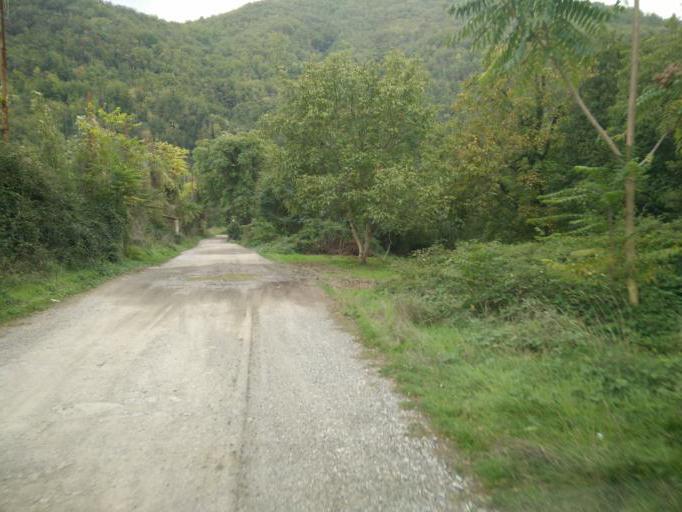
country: IT
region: Tuscany
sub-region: Provincia di Massa-Carrara
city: Casola in Lunigiana
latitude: 44.1989
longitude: 10.1730
